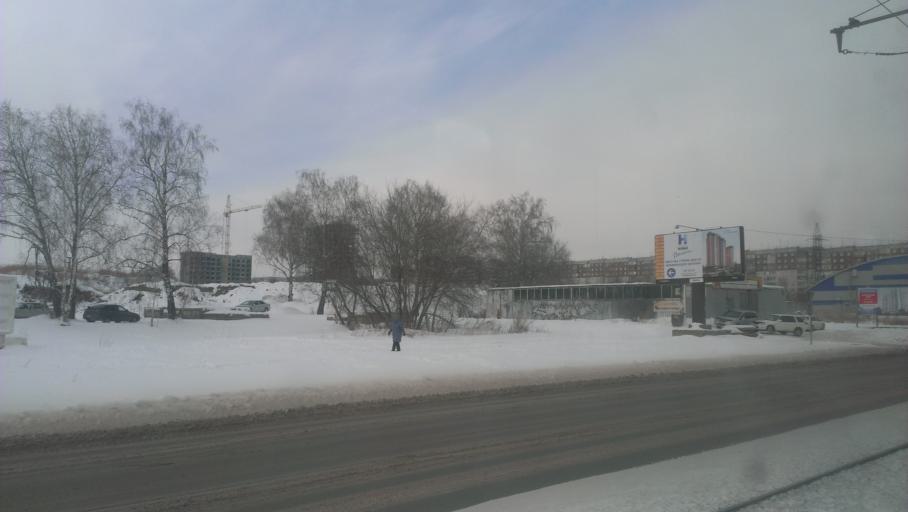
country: RU
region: Altai Krai
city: Novosilikatnyy
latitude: 53.3527
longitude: 83.6731
